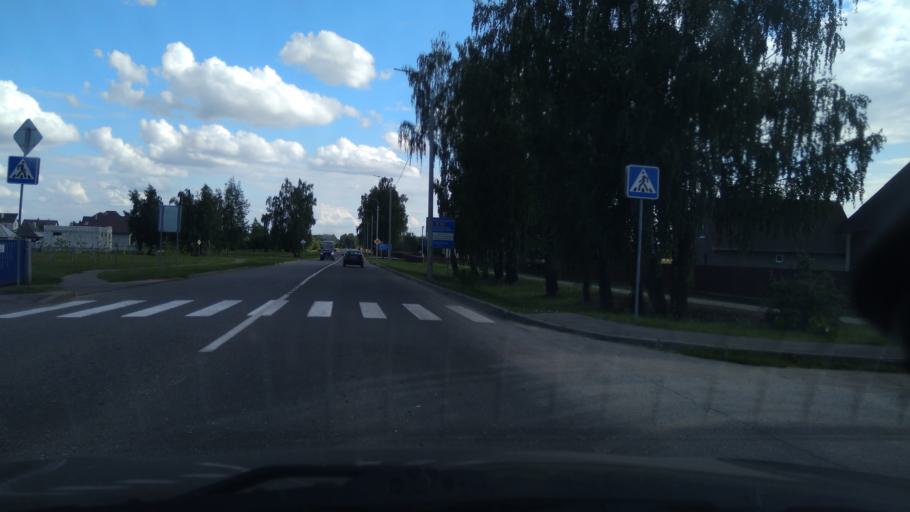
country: BY
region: Grodnenskaya
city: Masty
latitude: 53.3930
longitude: 24.5372
